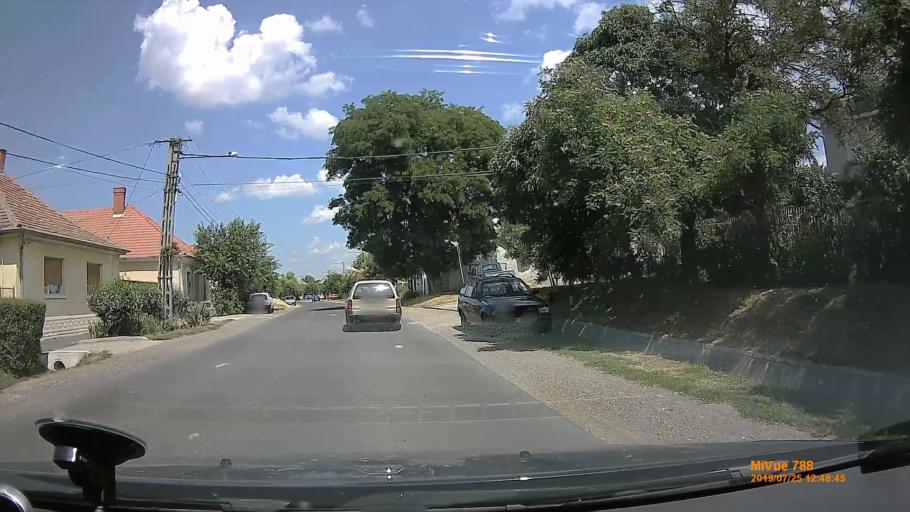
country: HU
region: Borsod-Abauj-Zemplen
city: Abaujszanto
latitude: 48.2710
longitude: 21.1841
